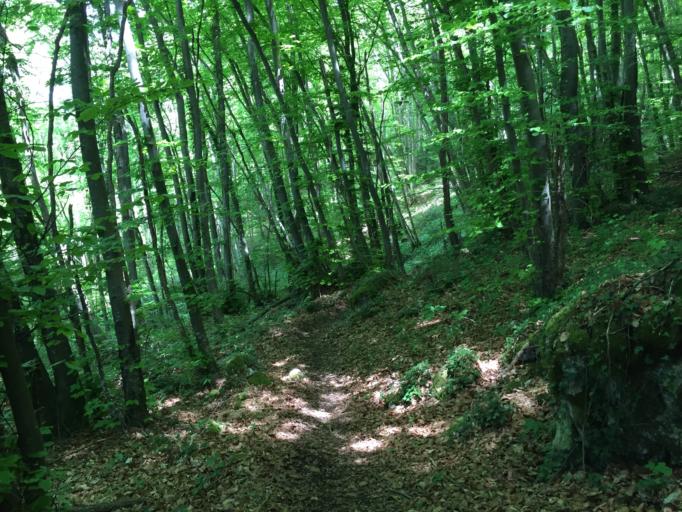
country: FR
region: Rhone-Alpes
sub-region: Departement de la Savoie
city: Mery
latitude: 45.6541
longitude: 5.9529
